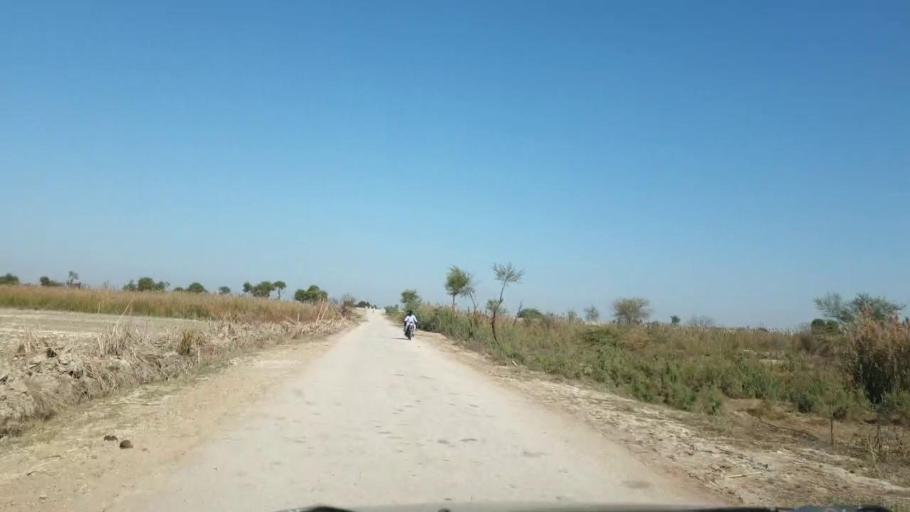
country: PK
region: Sindh
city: Sinjhoro
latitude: 26.1038
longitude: 68.8428
